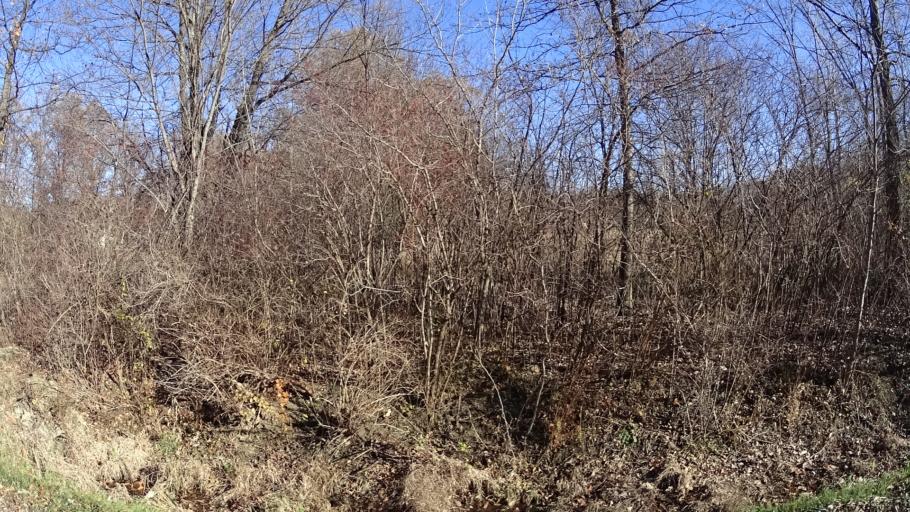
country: US
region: Ohio
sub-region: Lorain County
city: Avon Center
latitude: 41.4347
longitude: -81.9786
